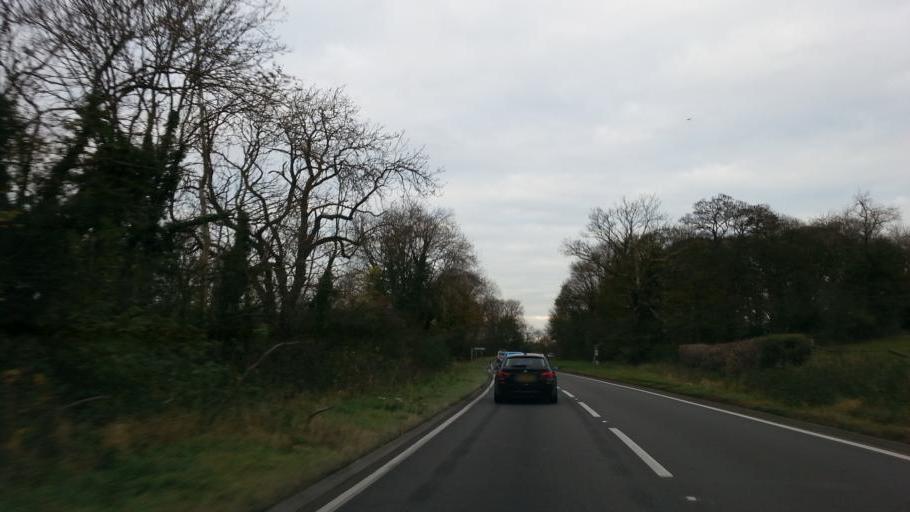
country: GB
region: England
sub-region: District of Rutland
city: South Luffenham
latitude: 52.5506
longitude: -0.5810
